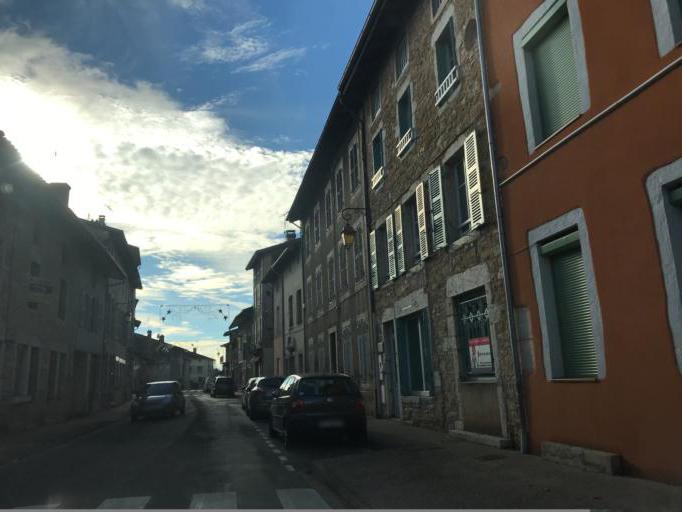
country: FR
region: Rhone-Alpes
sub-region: Departement de l'Ain
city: Saint-Jean-le-Vieux
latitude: 46.0286
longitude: 5.3886
